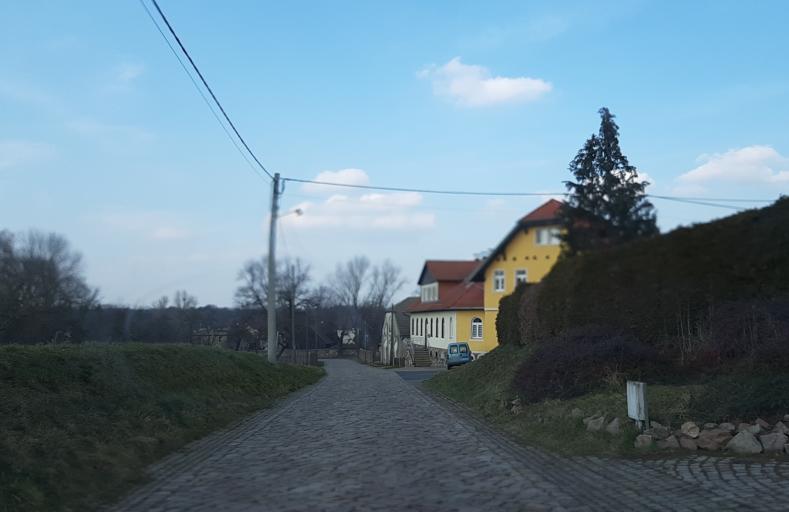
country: DE
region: Saxony
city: Wildenhain
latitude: 51.2877
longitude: 13.4766
